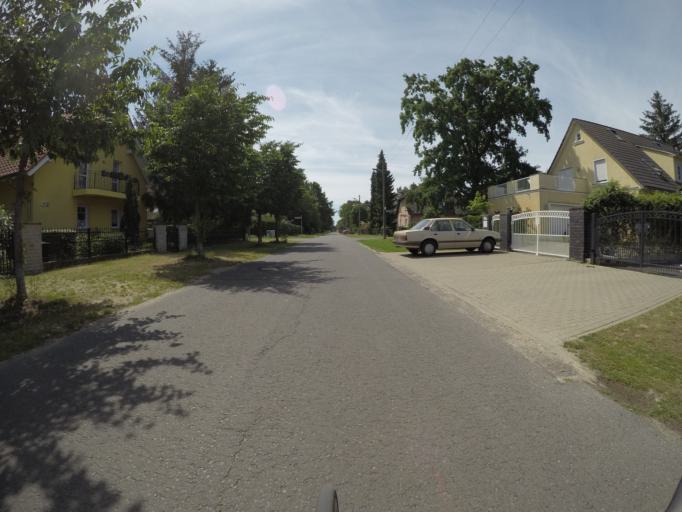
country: DE
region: Berlin
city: Mahlsdorf
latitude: 52.4802
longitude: 13.6120
